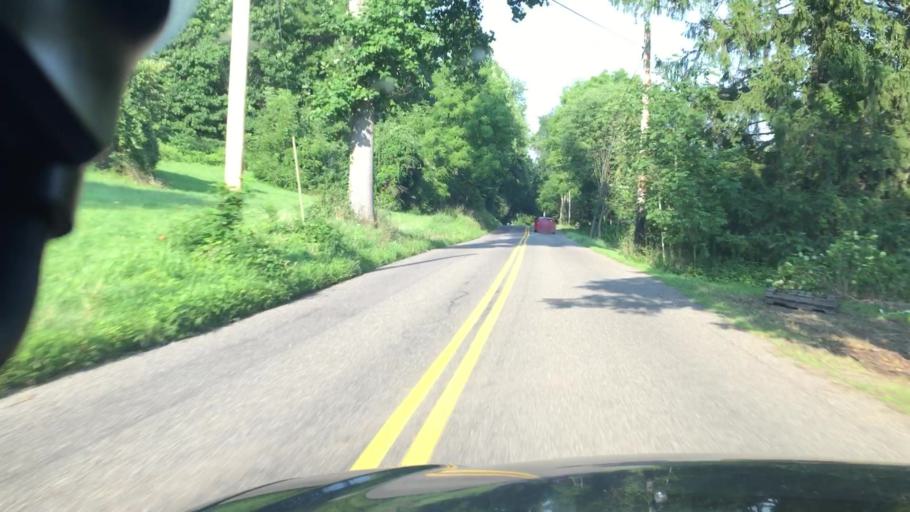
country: US
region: Pennsylvania
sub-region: Columbia County
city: Espy
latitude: 40.9719
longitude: -76.4125
